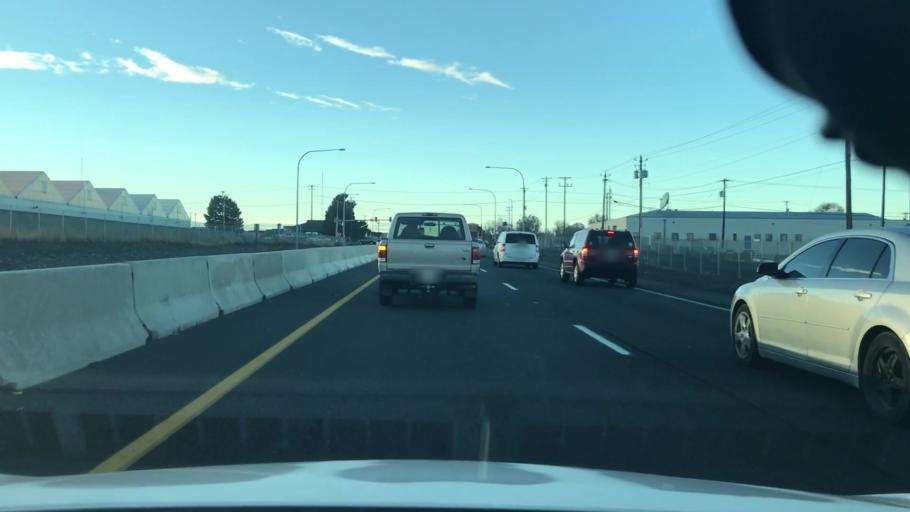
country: US
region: Washington
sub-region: Grant County
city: Moses Lake
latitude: 47.1332
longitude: -119.2569
